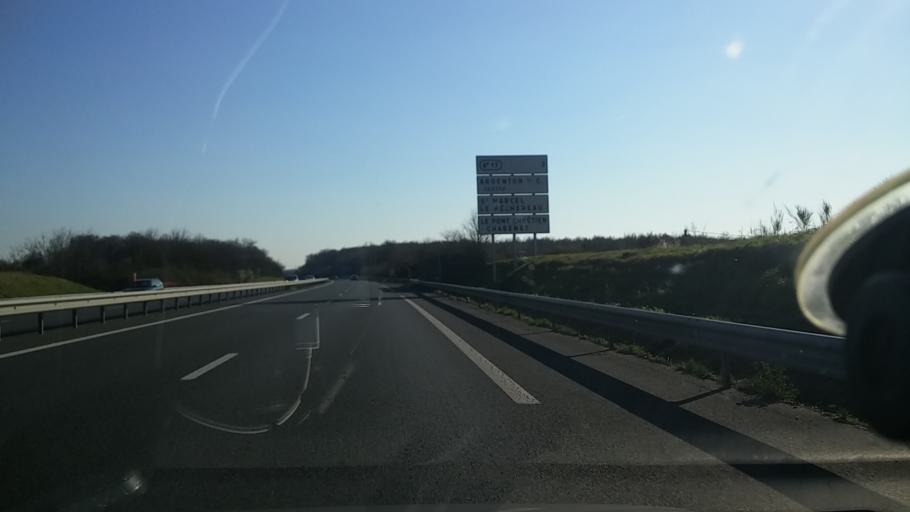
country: FR
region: Centre
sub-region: Departement de l'Indre
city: Saint-Marcel
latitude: 46.6457
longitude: 1.5550
